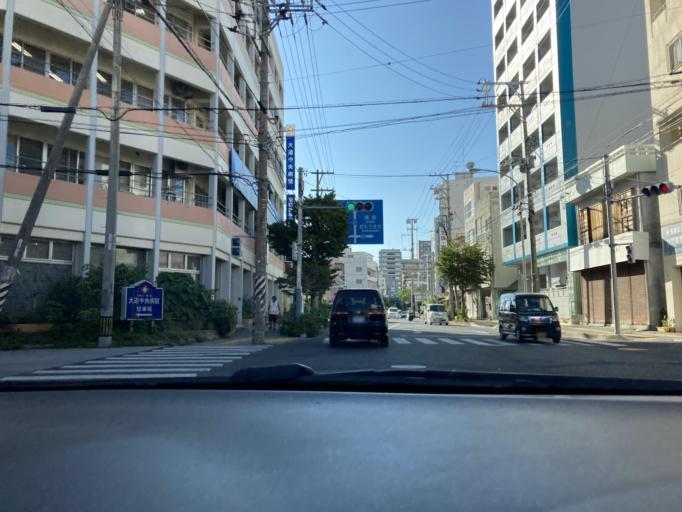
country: JP
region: Okinawa
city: Naha-shi
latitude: 26.2190
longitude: 127.6951
